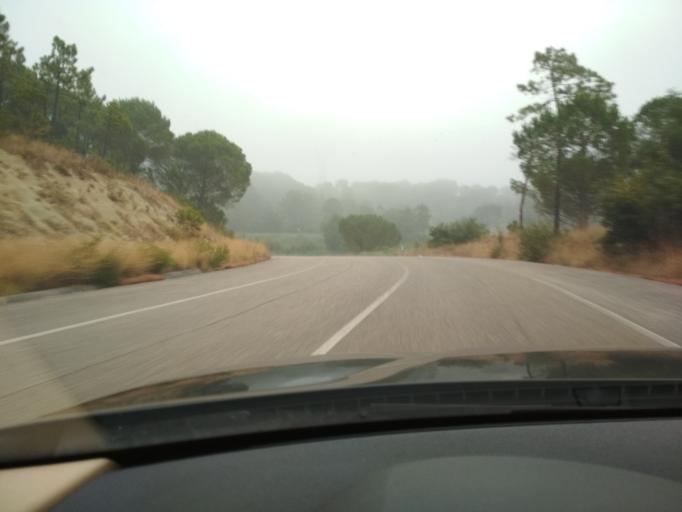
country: PT
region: Coimbra
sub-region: Condeixa-A-Nova
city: Condeixa-a-Nova
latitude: 40.1544
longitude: -8.4621
